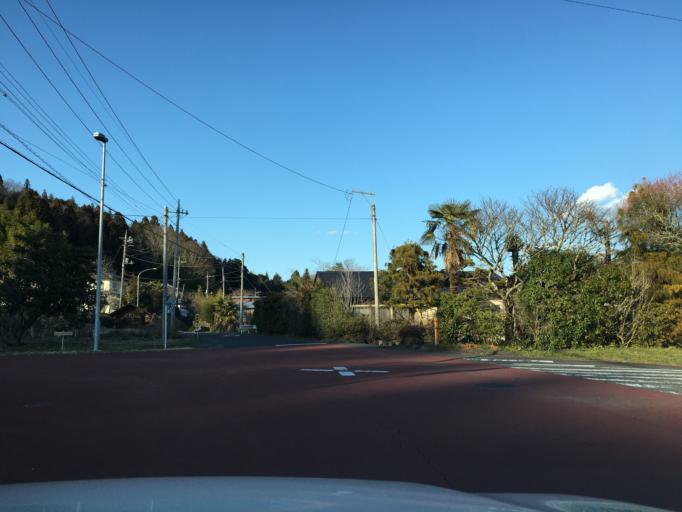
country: JP
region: Tochigi
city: Karasuyama
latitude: 36.7767
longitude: 140.2083
